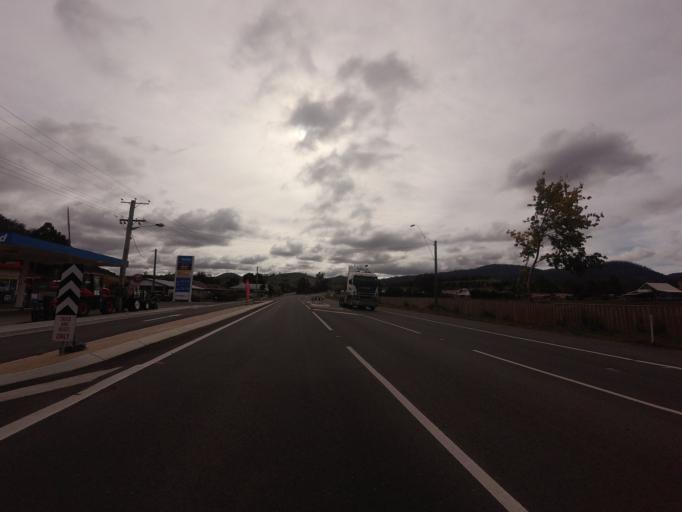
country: AU
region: Tasmania
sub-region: Brighton
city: Bridgewater
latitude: -42.6032
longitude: 147.2201
